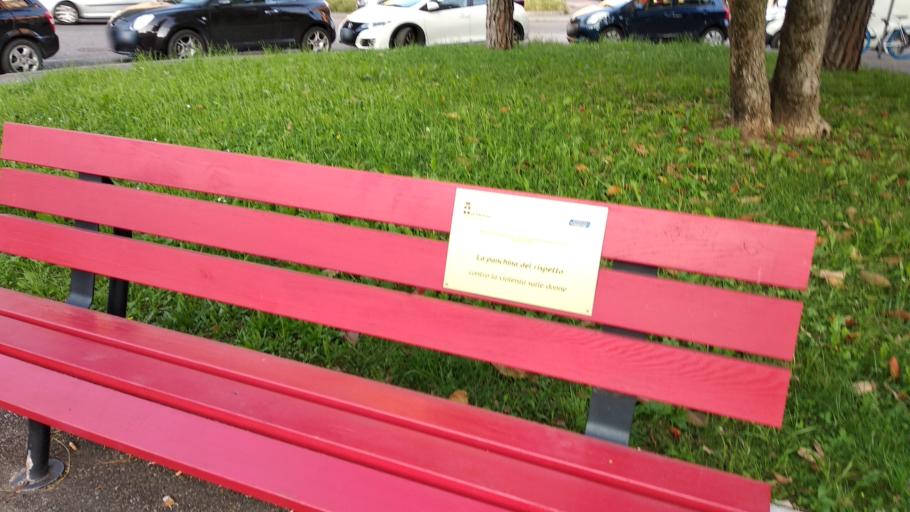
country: IT
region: Veneto
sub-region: Provincia di Verona
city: Verona
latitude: 45.4518
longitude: 10.9860
